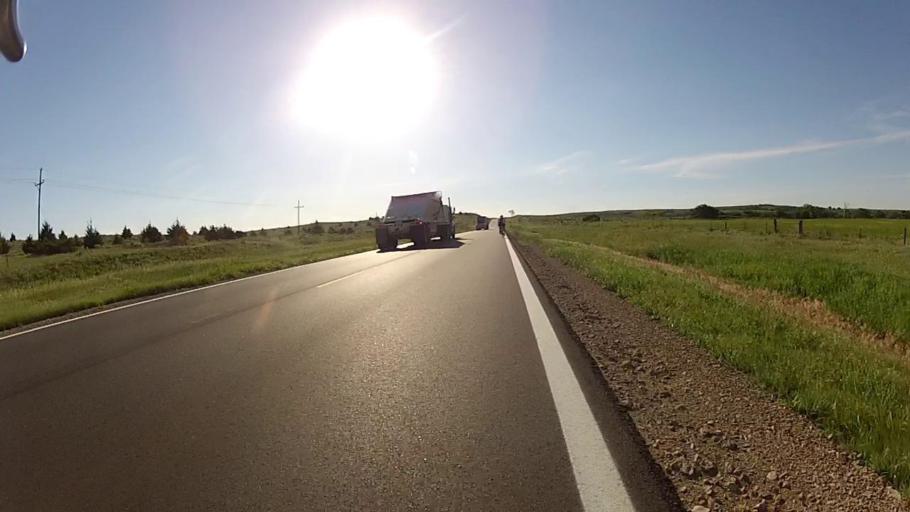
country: US
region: Kansas
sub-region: Comanche County
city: Coldwater
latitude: 37.2810
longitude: -99.0413
